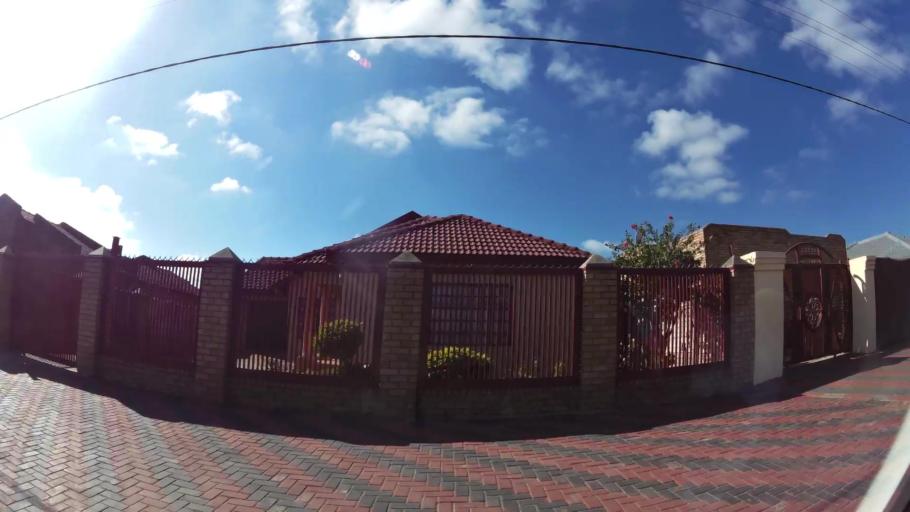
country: ZA
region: Limpopo
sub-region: Capricorn District Municipality
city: Polokwane
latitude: -23.8563
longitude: 29.3653
